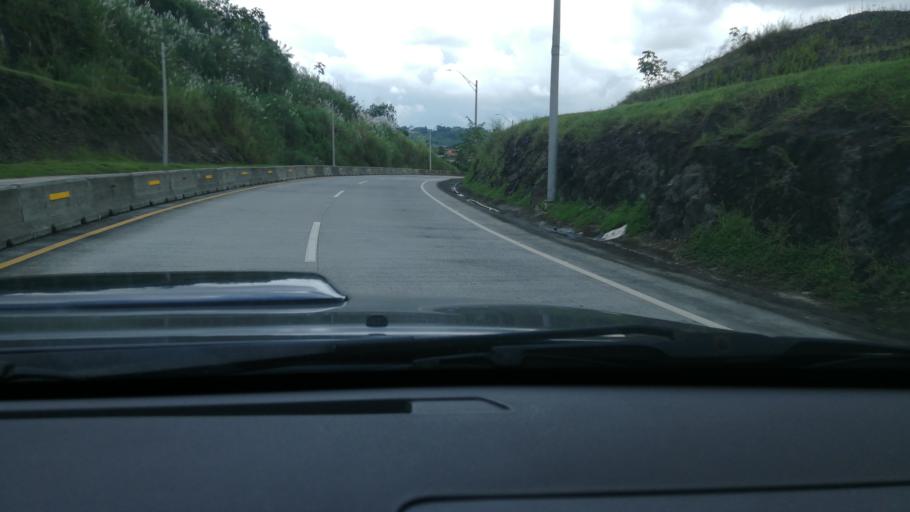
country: PA
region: Panama
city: San Miguelito
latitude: 9.0615
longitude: -79.4779
